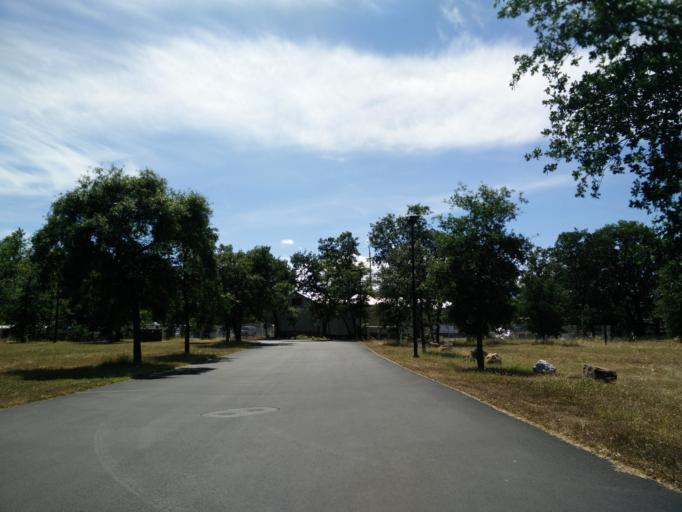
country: US
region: California
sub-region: Shasta County
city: Redding
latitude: 40.5945
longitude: -122.3869
